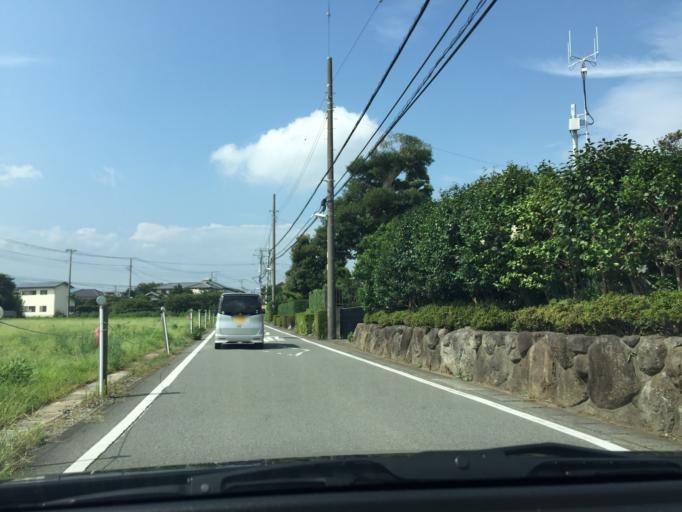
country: JP
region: Shizuoka
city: Mishima
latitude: 35.1417
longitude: 138.8998
